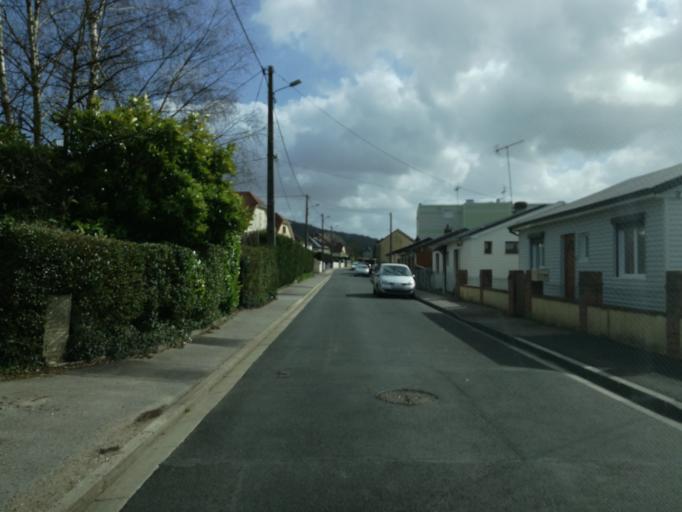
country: FR
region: Haute-Normandie
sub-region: Departement de la Seine-Maritime
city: Le Trait
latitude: 49.4916
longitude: 0.7993
